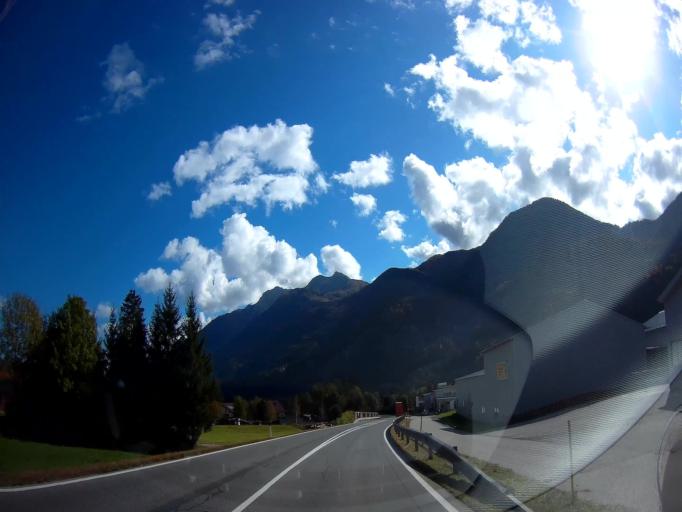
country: AT
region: Carinthia
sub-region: Politischer Bezirk Spittal an der Drau
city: Oberdrauburg
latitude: 46.7457
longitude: 12.9979
